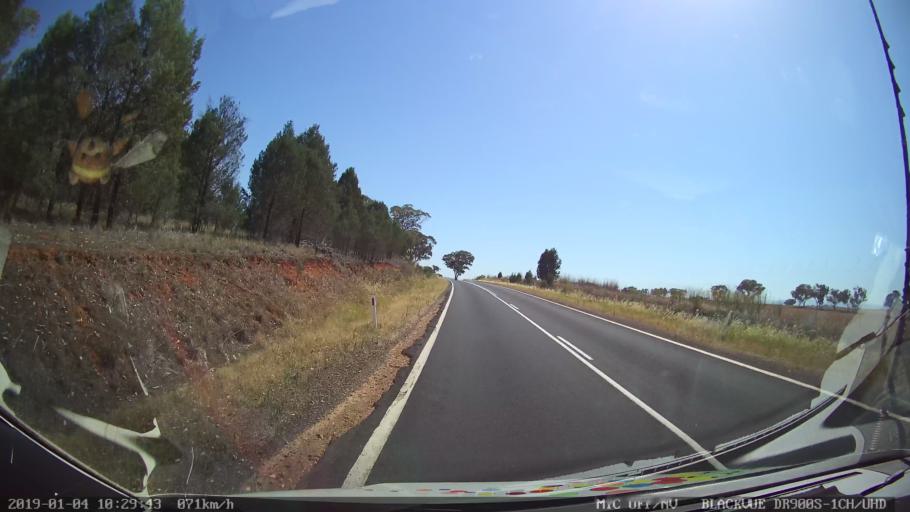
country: AU
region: New South Wales
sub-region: Cabonne
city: Canowindra
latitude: -33.3533
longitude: 148.6229
